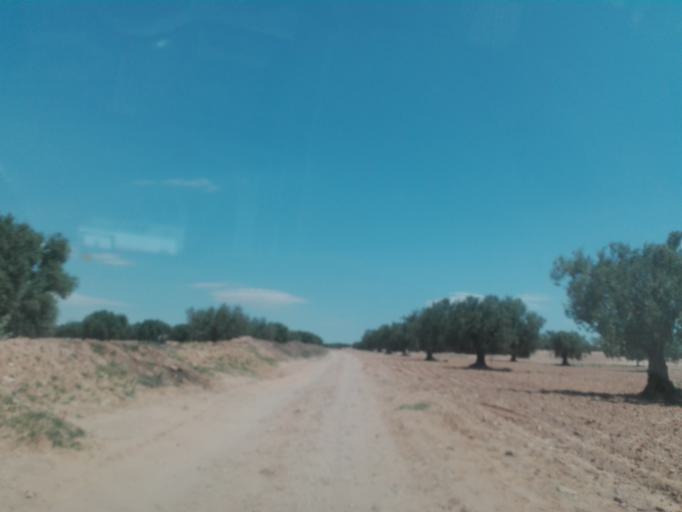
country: TN
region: Safaqis
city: Sfax
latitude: 34.6590
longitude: 10.6005
